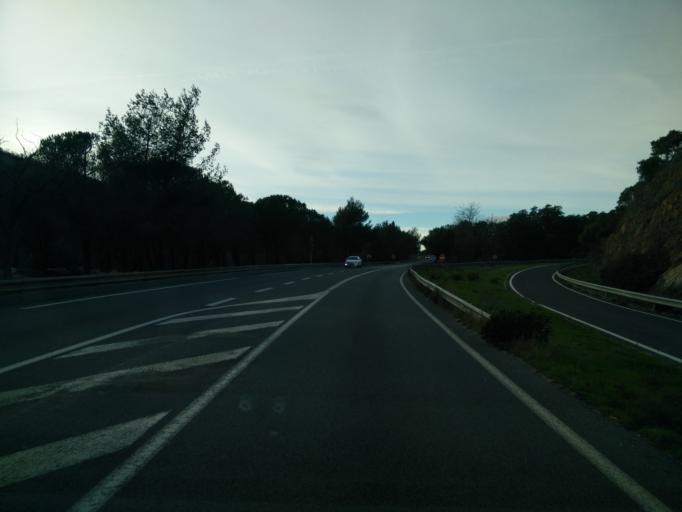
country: FR
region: Provence-Alpes-Cote d'Azur
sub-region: Departement du Var
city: Bormes-les-Mimosas
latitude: 43.1498
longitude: 6.2924
